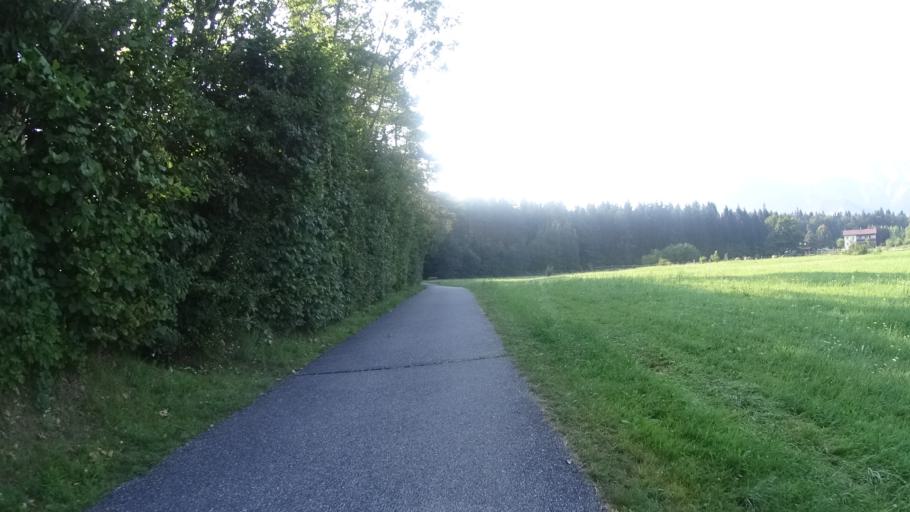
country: AT
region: Carinthia
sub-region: Politischer Bezirk Klagenfurt Land
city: Ludmannsdorf
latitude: 46.5351
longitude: 14.1141
